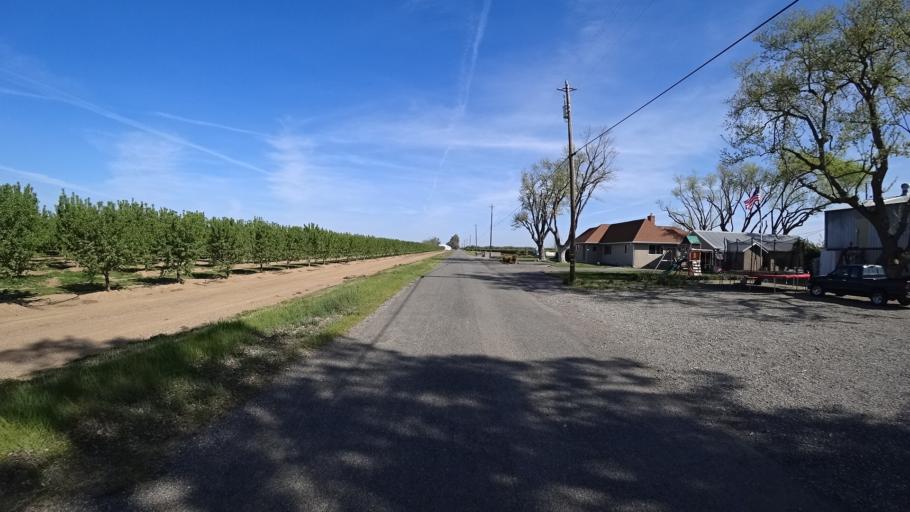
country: US
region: California
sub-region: Glenn County
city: Willows
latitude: 39.6313
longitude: -122.2160
